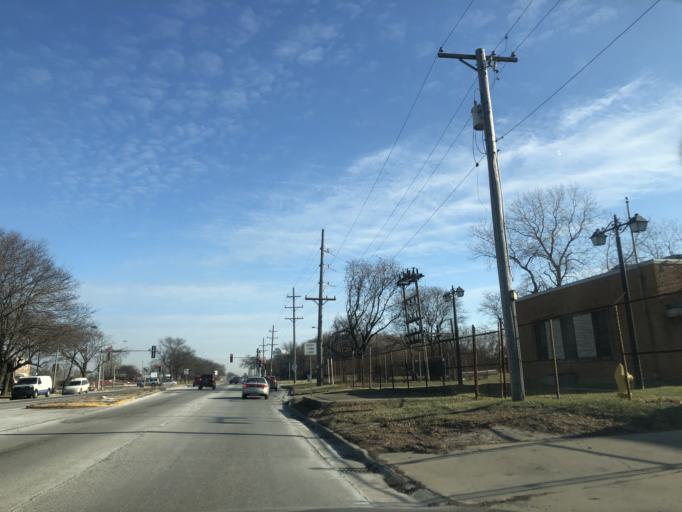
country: US
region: Illinois
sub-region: Cook County
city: Stickney
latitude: 41.8217
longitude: -87.7647
